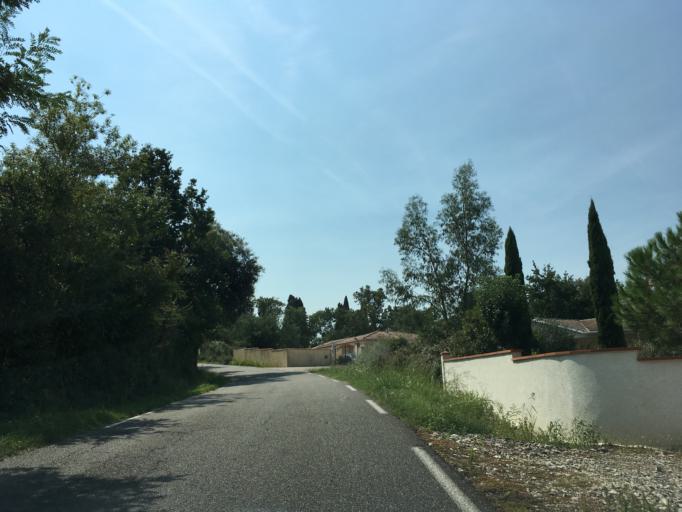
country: FR
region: Midi-Pyrenees
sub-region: Departement du Tarn-et-Garonne
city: Saint-Nauphary
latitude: 43.9928
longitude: 1.4220
